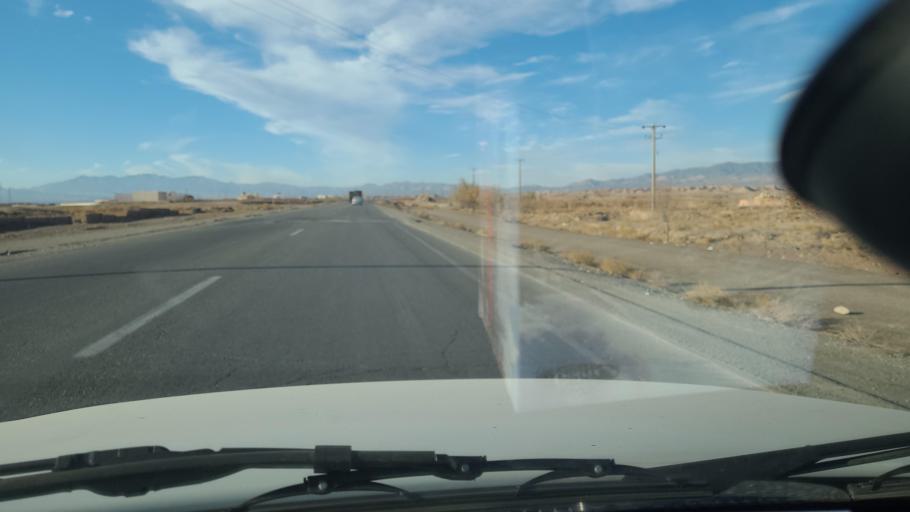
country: IR
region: Razavi Khorasan
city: Sabzevar
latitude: 36.2353
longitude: 57.6444
